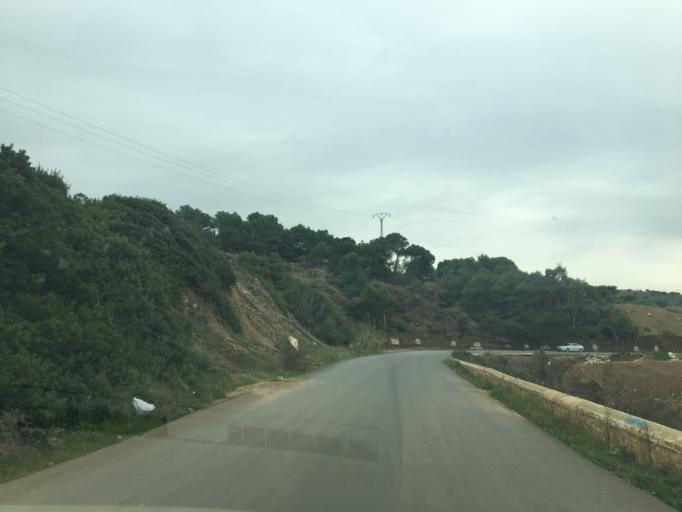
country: DZ
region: Tipaza
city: Tipasa
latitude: 36.6306
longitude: 2.2841
